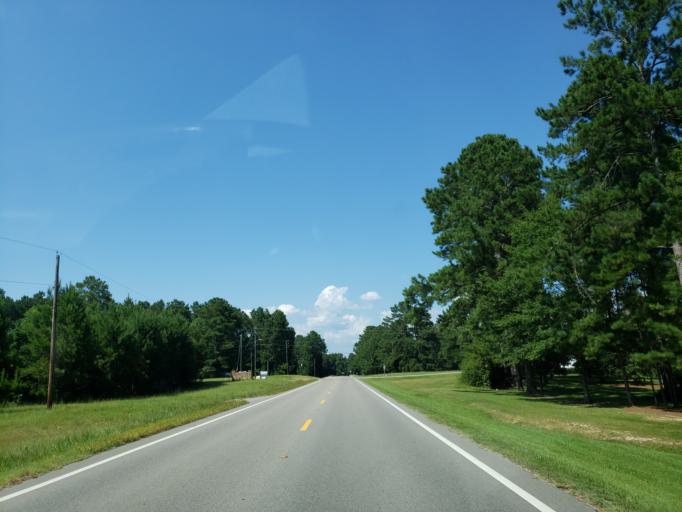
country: US
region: Mississippi
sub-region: Lamar County
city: Sumrall
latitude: 31.4292
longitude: -89.5435
